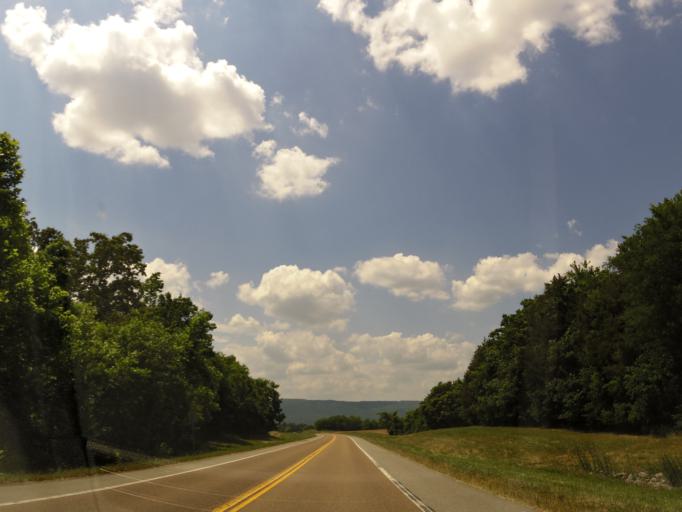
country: US
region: Tennessee
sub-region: Bledsoe County
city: Pikeville
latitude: 35.5832
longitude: -85.1707
